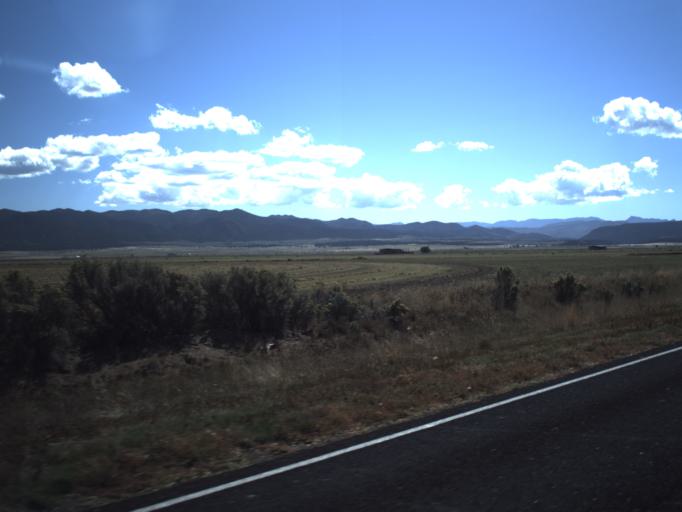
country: US
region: Utah
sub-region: Washington County
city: Enterprise
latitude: 37.6443
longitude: -113.6612
